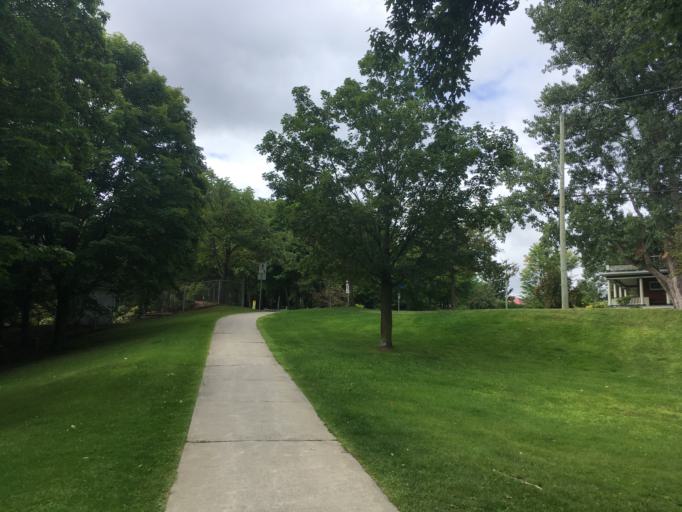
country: CA
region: Quebec
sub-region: Estrie
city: Sherbrooke
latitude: 45.4018
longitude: -71.9043
